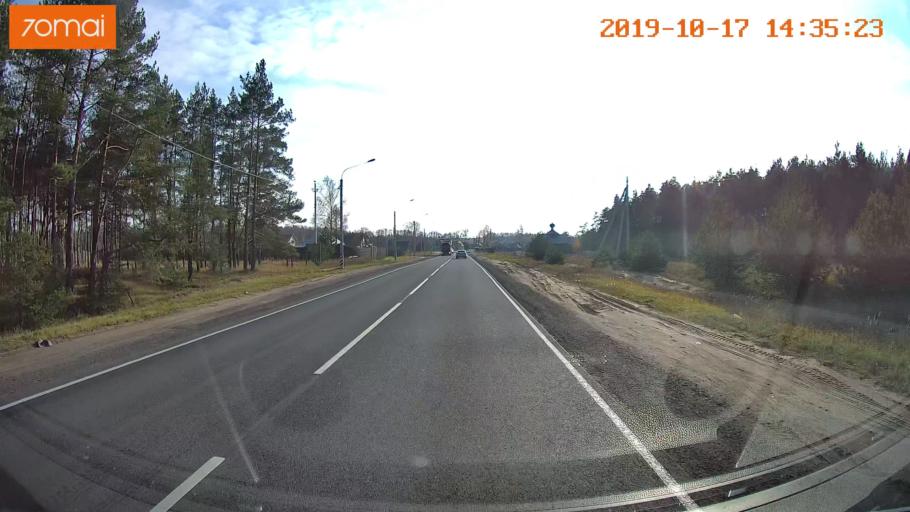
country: RU
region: Rjazan
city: Solotcha
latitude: 54.9005
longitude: 40.0025
